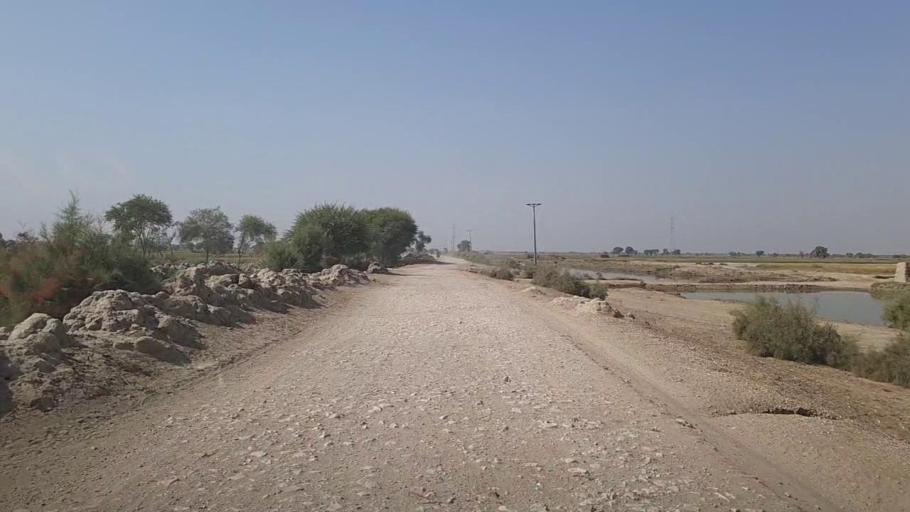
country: PK
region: Sindh
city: Kandhkot
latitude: 28.4063
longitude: 69.2529
